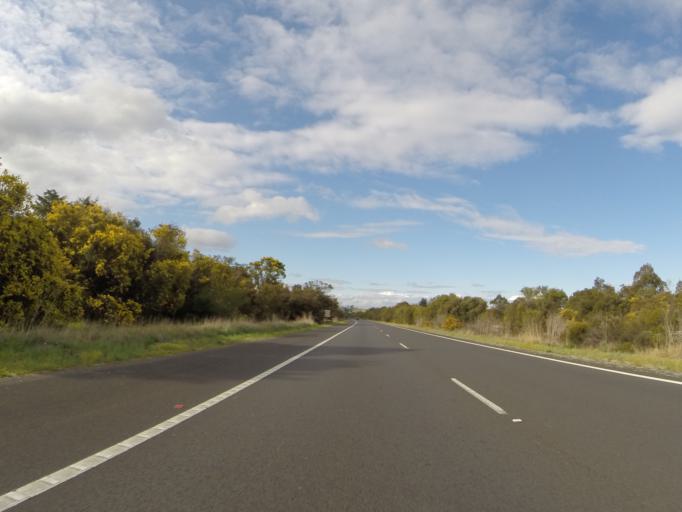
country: AU
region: New South Wales
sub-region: Wingecarribee
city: Bundanoon
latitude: -34.5940
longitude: 150.2428
